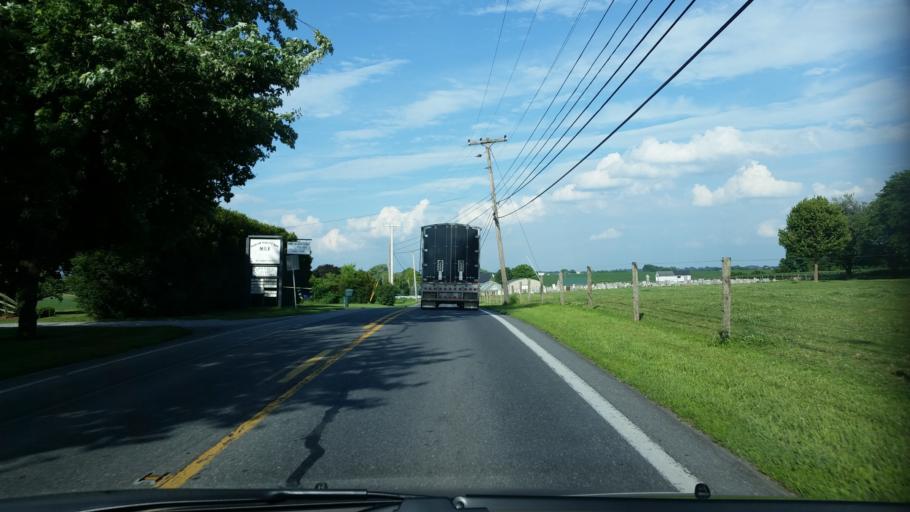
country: US
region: Pennsylvania
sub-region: Lancaster County
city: Salunga
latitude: 40.1288
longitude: -76.4479
